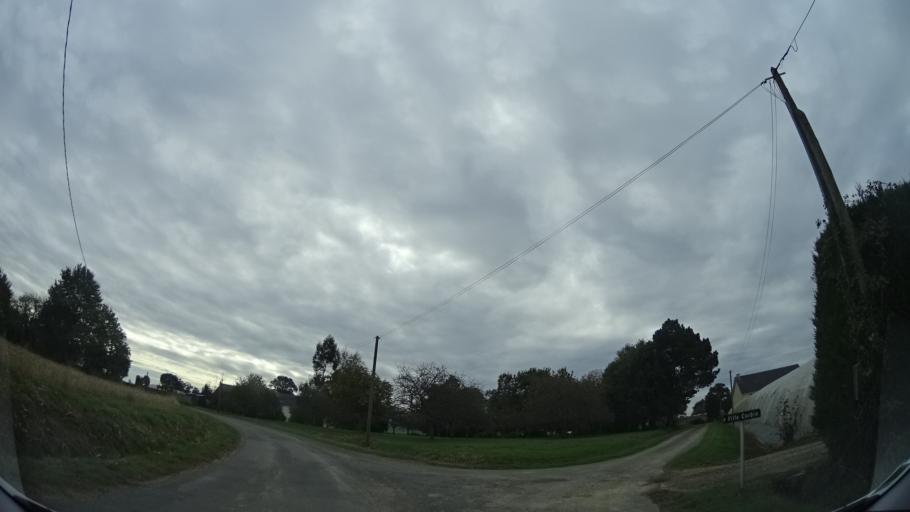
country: FR
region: Brittany
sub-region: Departement d'Ille-et-Vilaine
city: Vignoc
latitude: 48.2360
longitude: -1.7789
